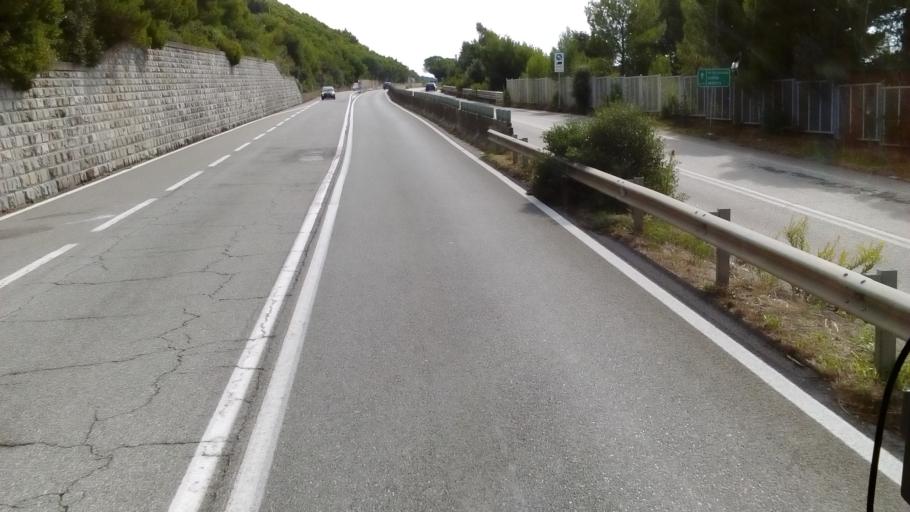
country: IT
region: Tuscany
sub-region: Provincia di Livorno
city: Quercianella
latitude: 43.4475
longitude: 10.3815
